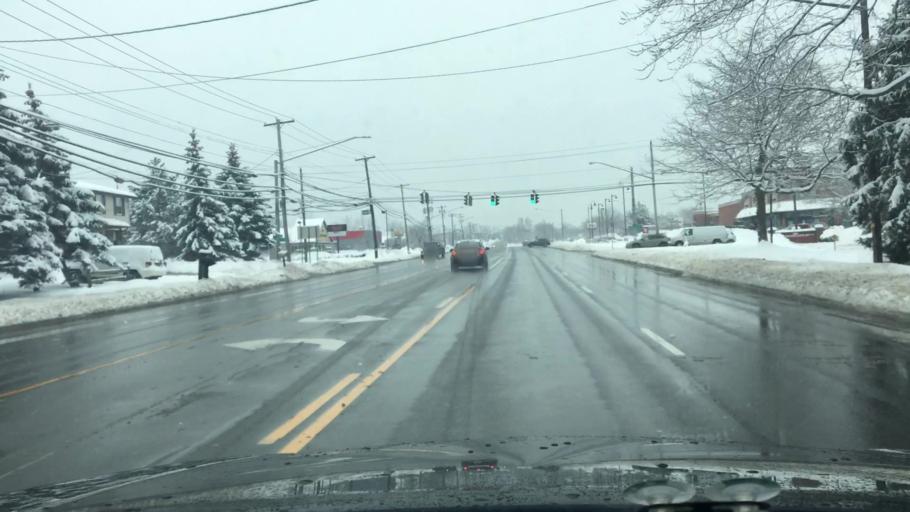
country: US
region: New York
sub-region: Erie County
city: Orchard Park
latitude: 42.8046
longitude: -78.7518
